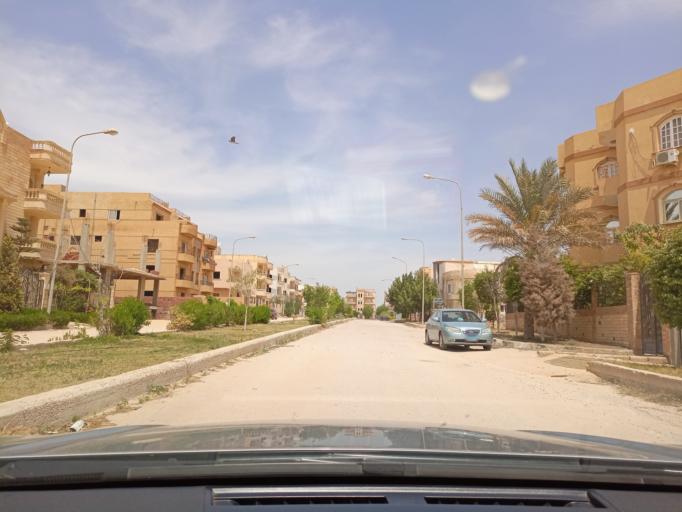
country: EG
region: Muhafazat al Qalyubiyah
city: Al Khankah
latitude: 30.2313
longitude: 31.4889
